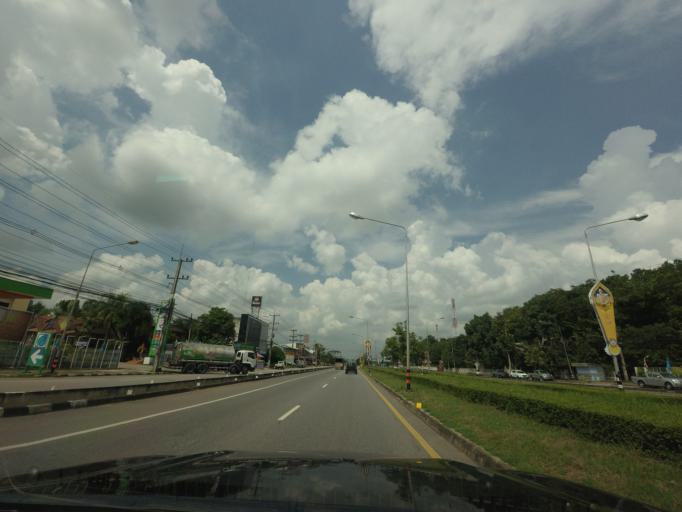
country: TH
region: Khon Kaen
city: Nong Ruea
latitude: 16.4905
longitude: 102.4427
